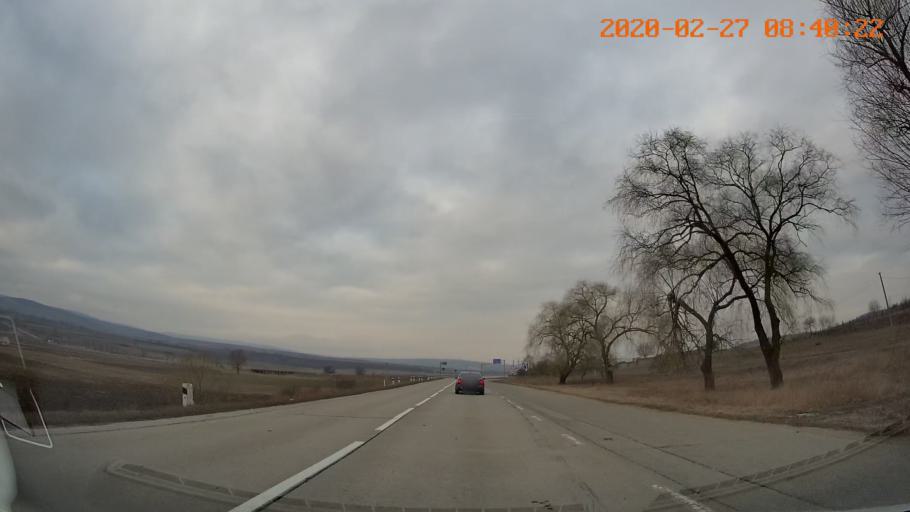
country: MD
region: Taraclia
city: Telenesti
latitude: 47.3894
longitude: 28.3690
